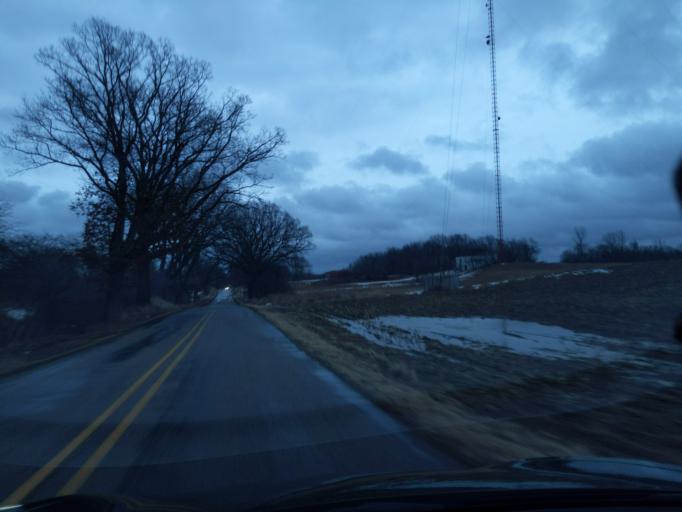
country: US
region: Michigan
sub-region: Eaton County
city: Eaton Rapids
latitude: 42.4438
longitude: -84.5755
